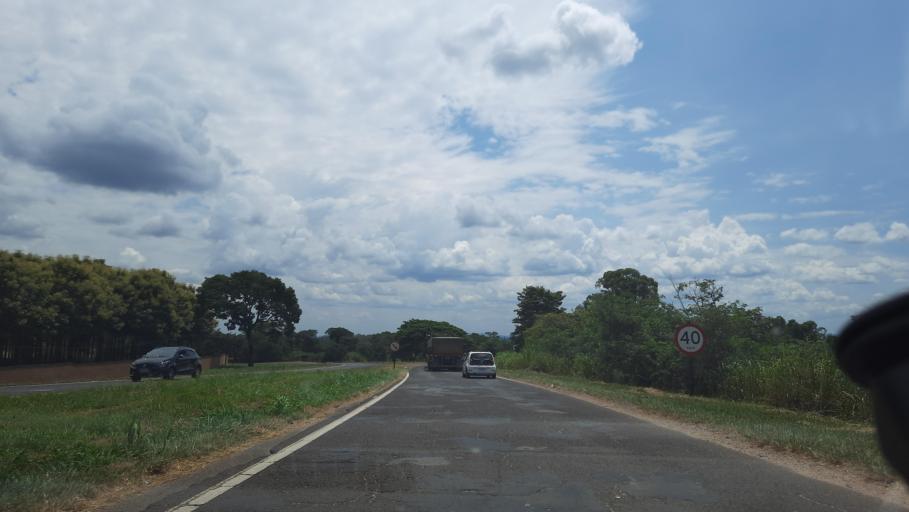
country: BR
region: Sao Paulo
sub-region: Mococa
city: Mococa
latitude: -21.5176
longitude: -47.0309
